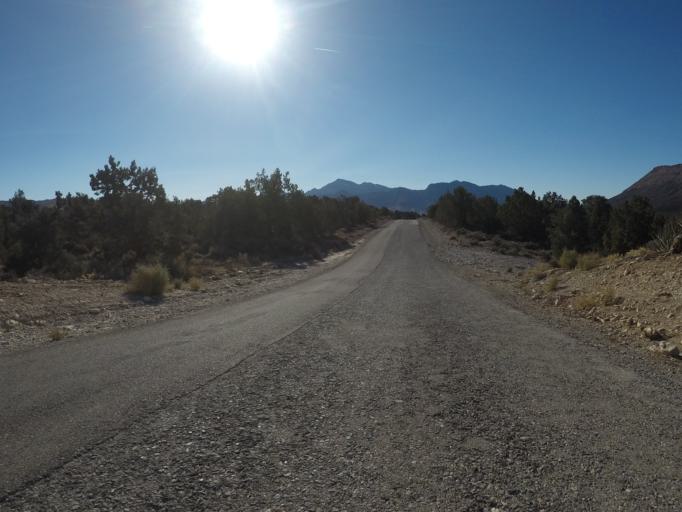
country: US
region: Nevada
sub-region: Clark County
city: Summerlin South
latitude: 36.0662
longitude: -115.5609
